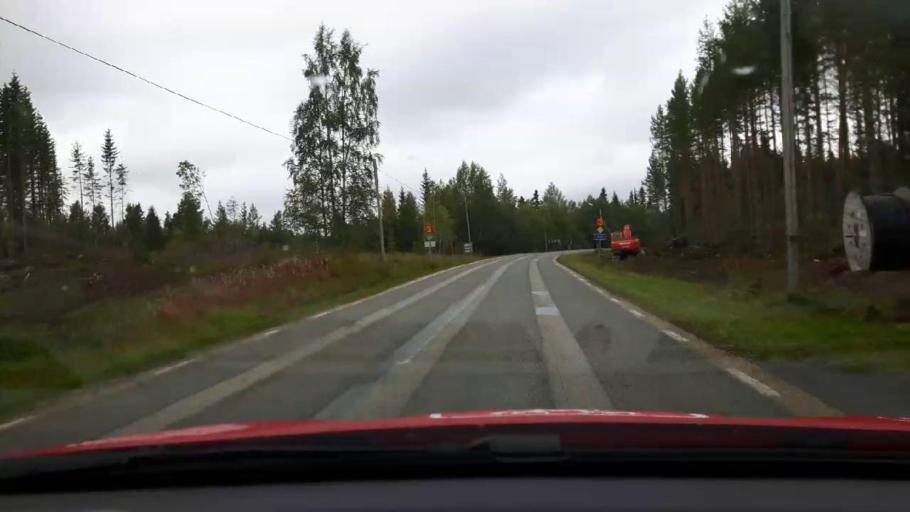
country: SE
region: Jaemtland
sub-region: Bergs Kommun
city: Hoverberg
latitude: 62.8164
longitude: 14.4030
